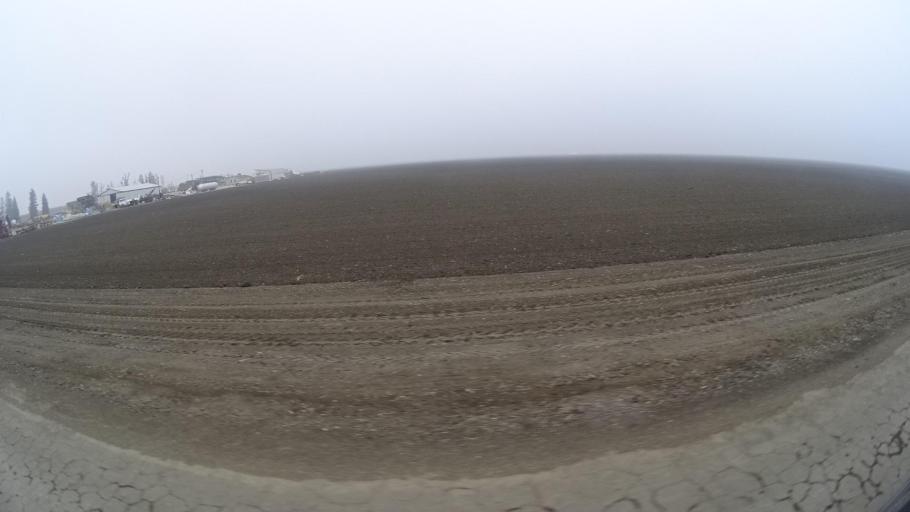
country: US
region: California
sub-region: Kern County
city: Buttonwillow
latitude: 35.4121
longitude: -119.5159
